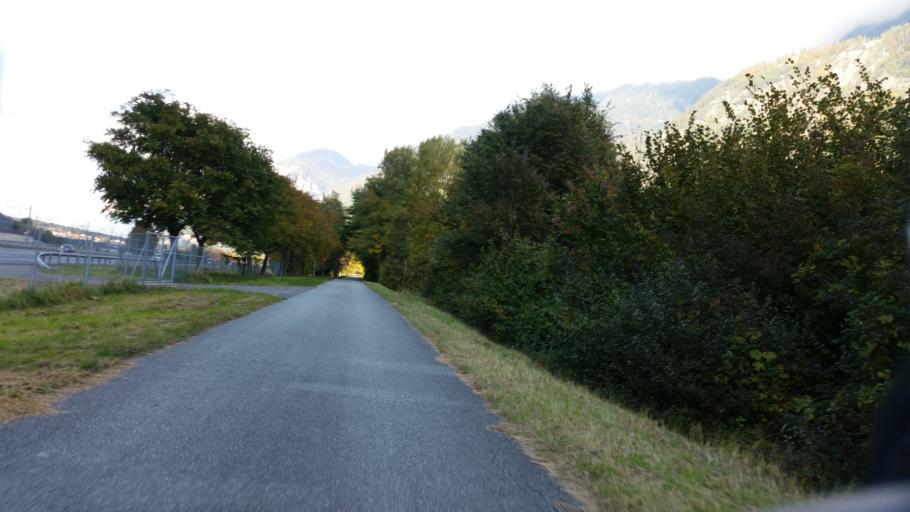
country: CH
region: Valais
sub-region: Saint-Maurice District
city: Vernayaz
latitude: 46.1545
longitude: 7.0321
